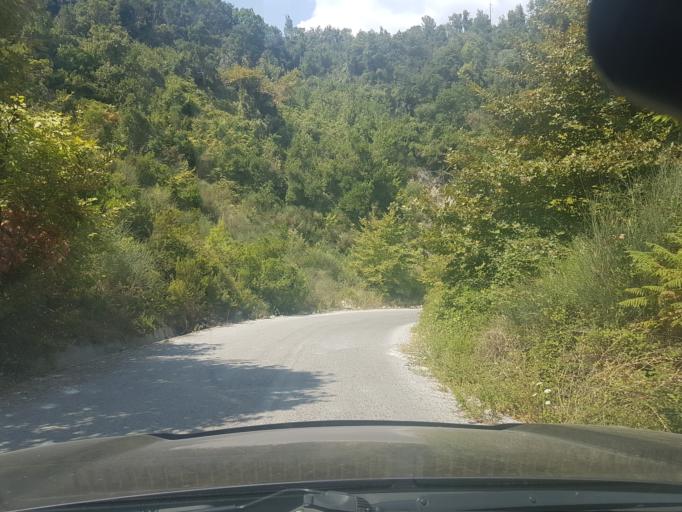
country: GR
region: Central Greece
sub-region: Nomos Evvoias
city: Kymi
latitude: 38.6535
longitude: 23.9219
